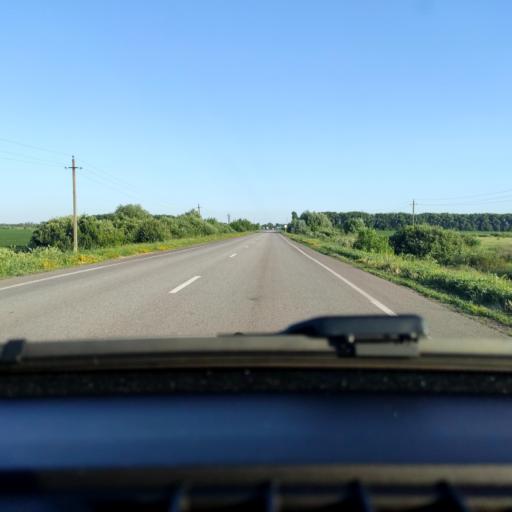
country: RU
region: Voronezj
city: Kashirskoye
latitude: 51.4736
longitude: 39.8609
